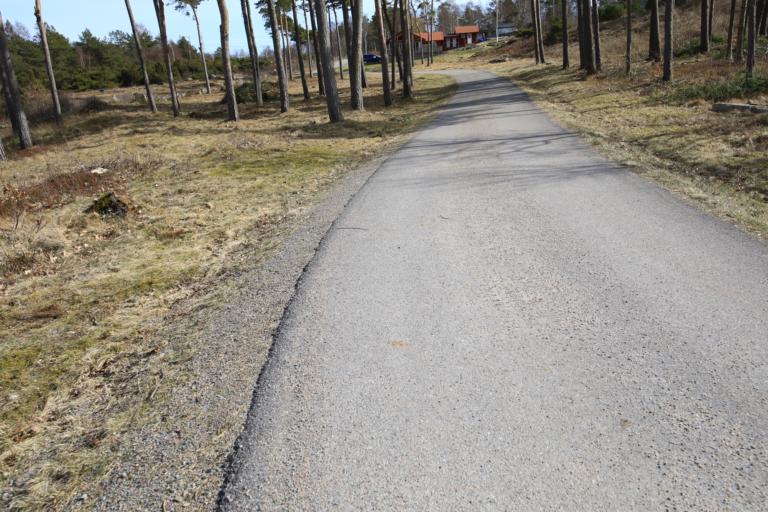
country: SE
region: Halland
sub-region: Kungsbacka Kommun
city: Frillesas
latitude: 57.2704
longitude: 12.1164
